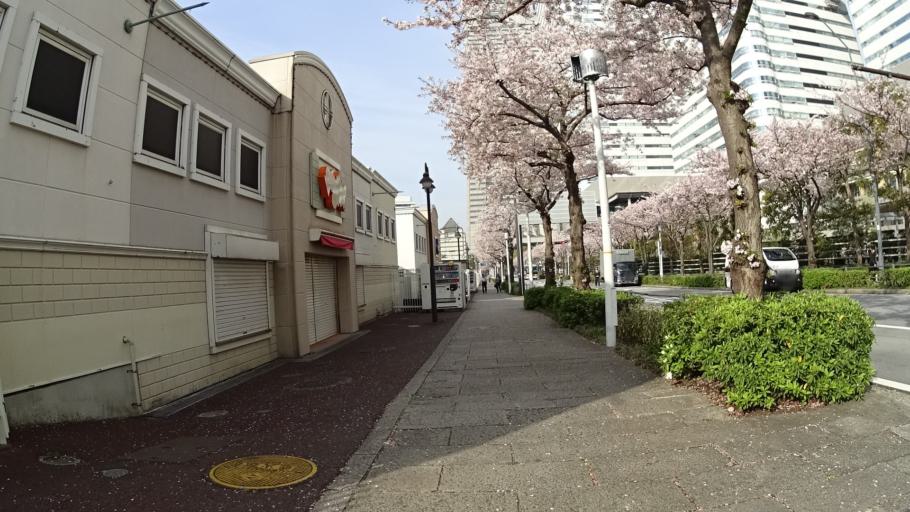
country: JP
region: Kanagawa
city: Yokohama
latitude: 35.4565
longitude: 139.6355
